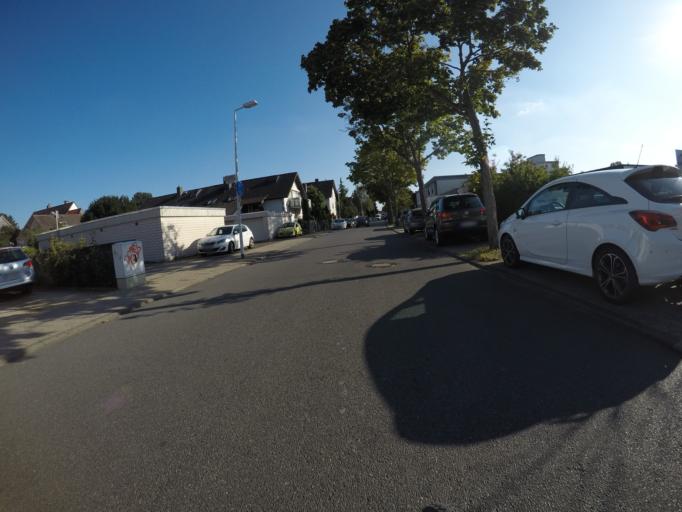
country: DE
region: Hesse
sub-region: Regierungsbezirk Darmstadt
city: Erzhausen
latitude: 49.9176
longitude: 8.6532
